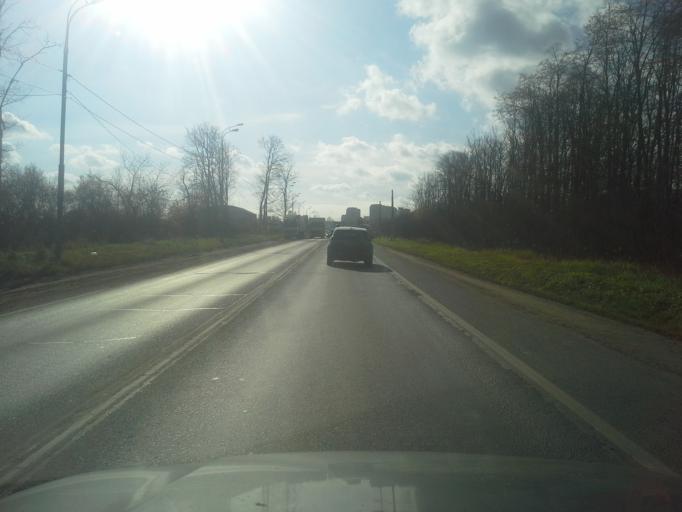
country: RU
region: Moskovskaya
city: Bol'shiye Vyazemy
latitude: 55.6344
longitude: 36.9838
